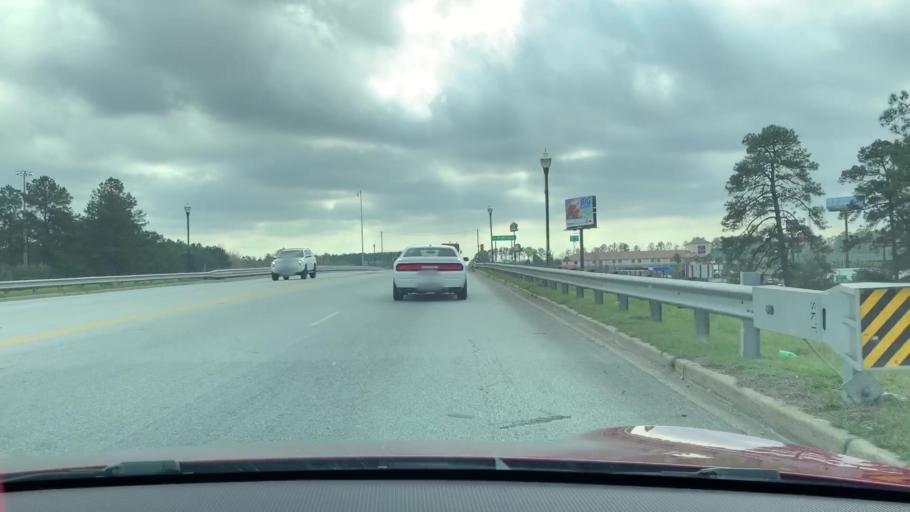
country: US
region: South Carolina
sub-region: Jasper County
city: Hardeeville
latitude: 32.2741
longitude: -81.0808
